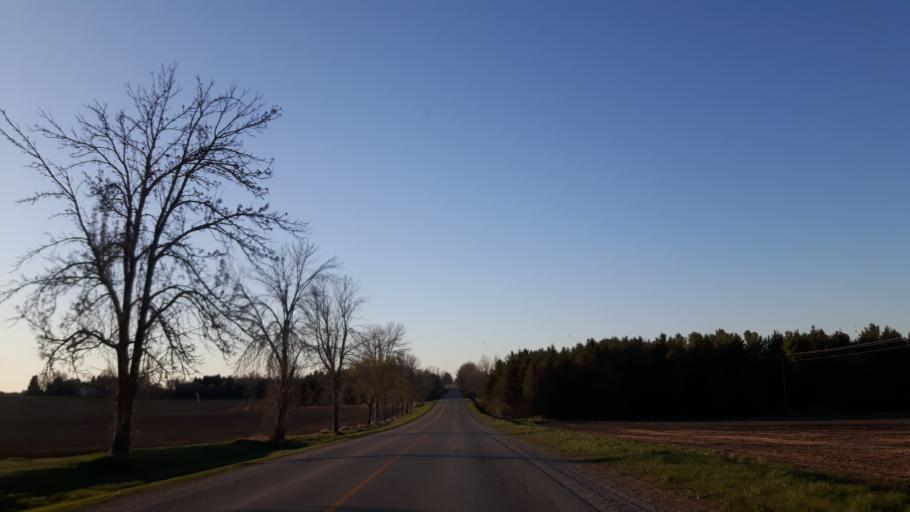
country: CA
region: Ontario
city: Bluewater
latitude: 43.5363
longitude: -81.5452
